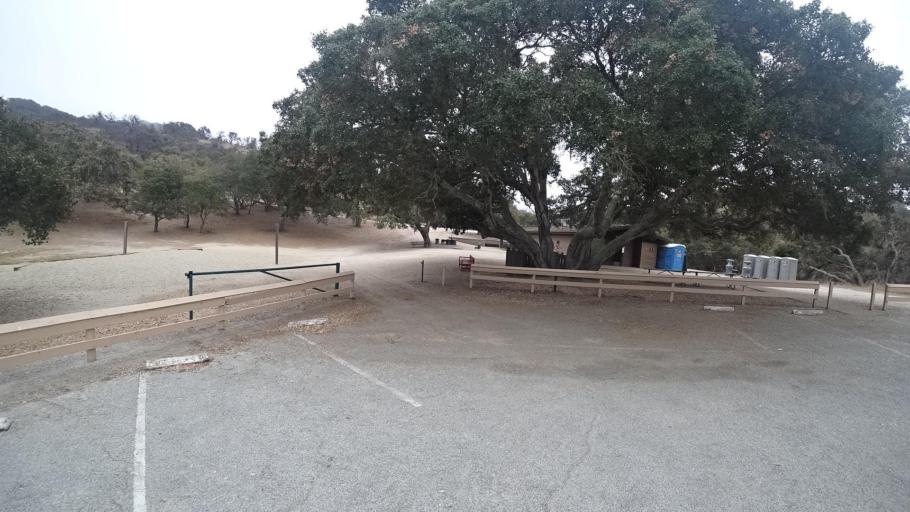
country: US
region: California
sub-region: Monterey County
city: Salinas
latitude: 36.5857
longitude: -121.6891
